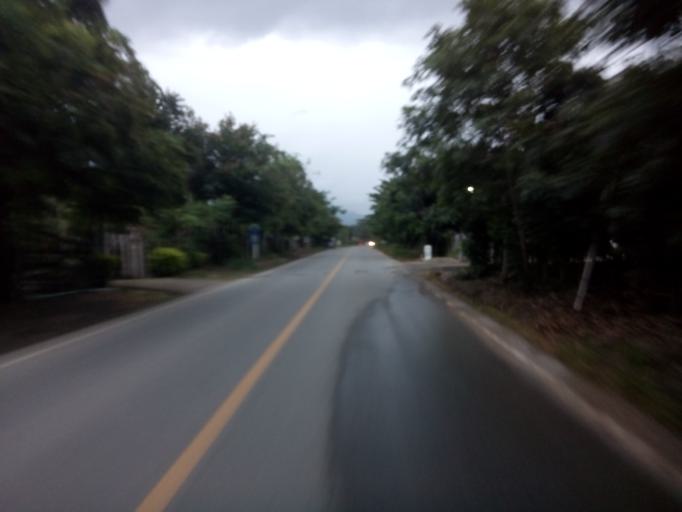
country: TH
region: Chiang Mai
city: Mae Wang
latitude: 18.6095
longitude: 98.7811
